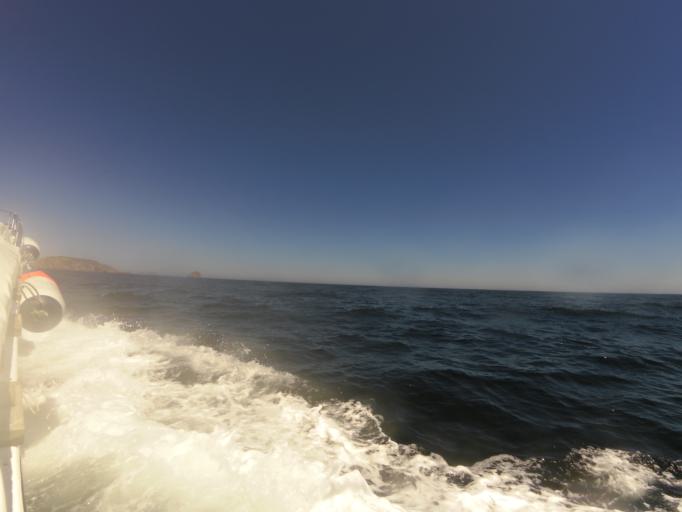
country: PT
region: Leiria
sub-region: Peniche
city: Peniche
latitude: 39.3997
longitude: -9.4865
